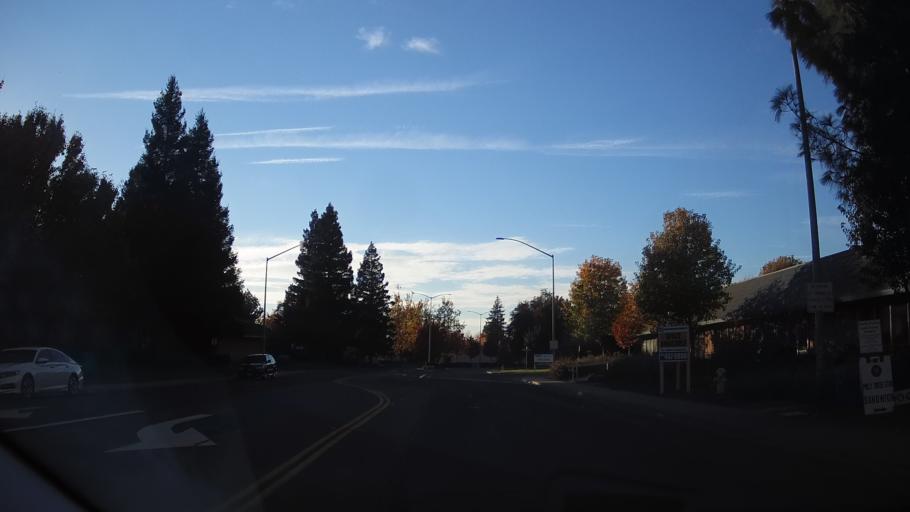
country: US
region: California
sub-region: Yolo County
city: West Sacramento
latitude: 38.5720
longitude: -121.5492
